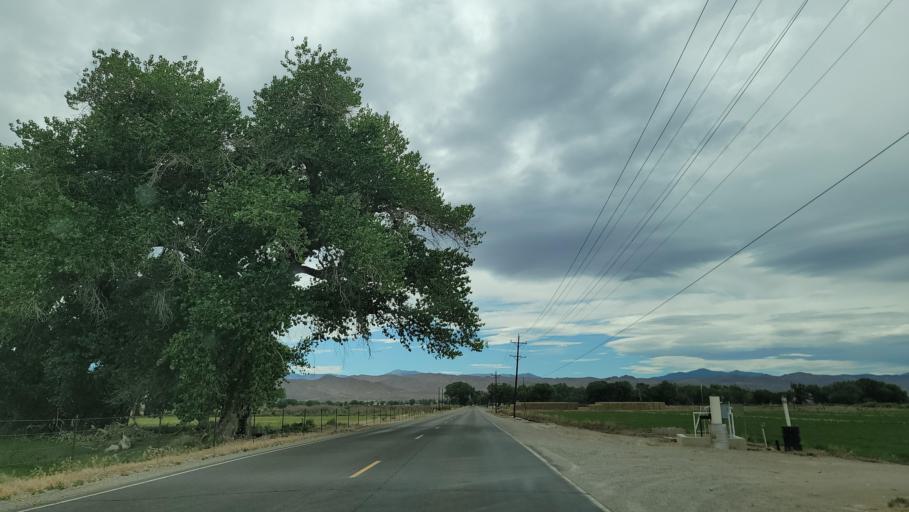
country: US
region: Nevada
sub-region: Lyon County
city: Yerington
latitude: 39.0481
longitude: -119.1694
